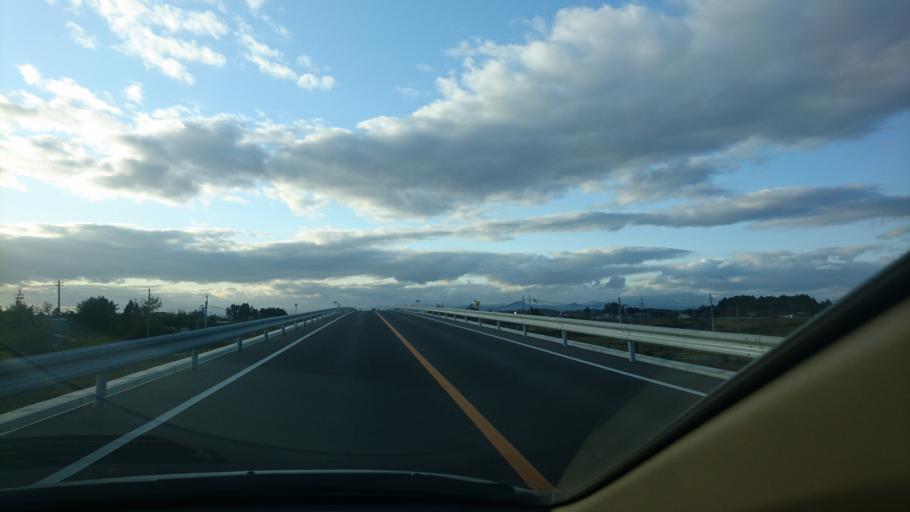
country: JP
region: Miyagi
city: Kogota
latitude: 38.7369
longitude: 141.0480
